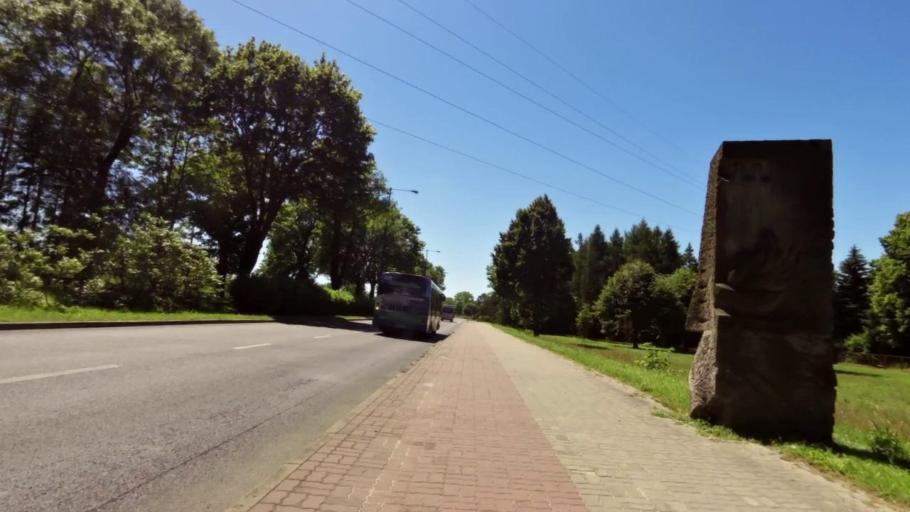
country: PL
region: West Pomeranian Voivodeship
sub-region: Powiat kolobrzeski
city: Kolobrzeg
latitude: 54.1571
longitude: 15.5650
